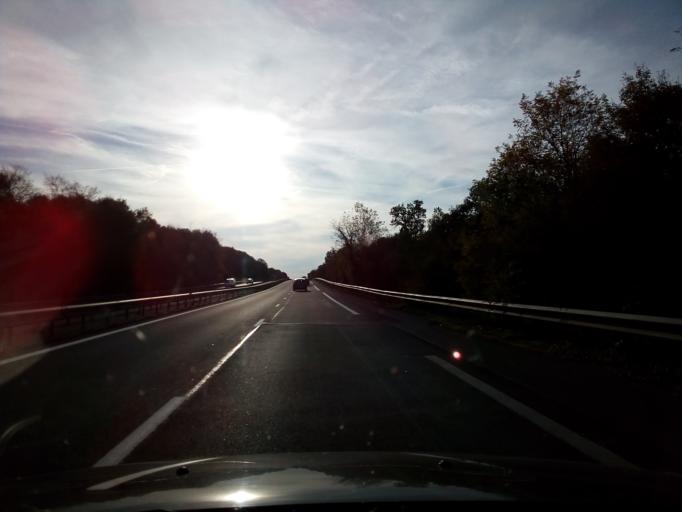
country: FR
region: Poitou-Charentes
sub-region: Departement de la Charente
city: Saint-Projet-Saint-Constant
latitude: 45.7244
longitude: 0.3227
